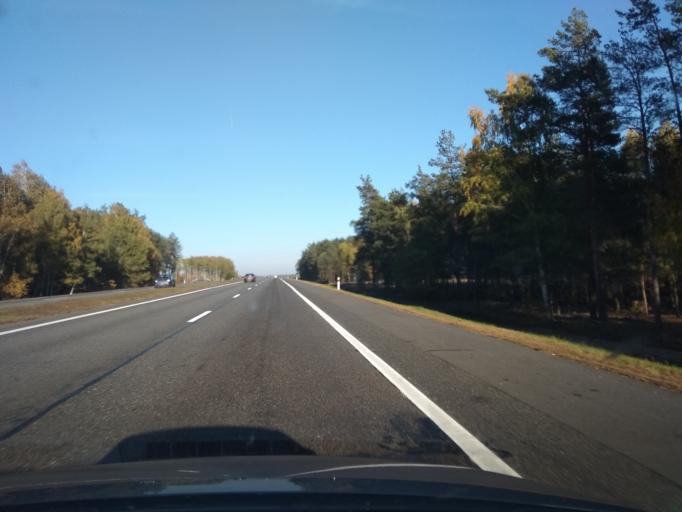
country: BY
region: Brest
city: Nyakhachava
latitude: 52.6571
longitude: 25.2696
